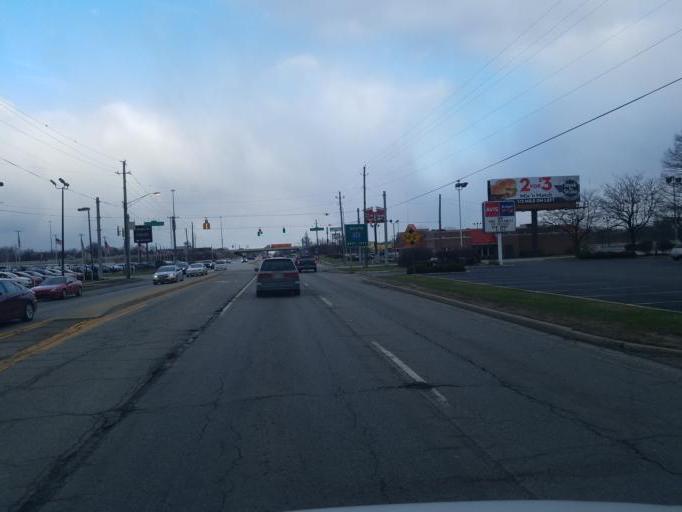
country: US
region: Indiana
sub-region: Marion County
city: Warren Park
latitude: 39.7726
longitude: -86.0351
